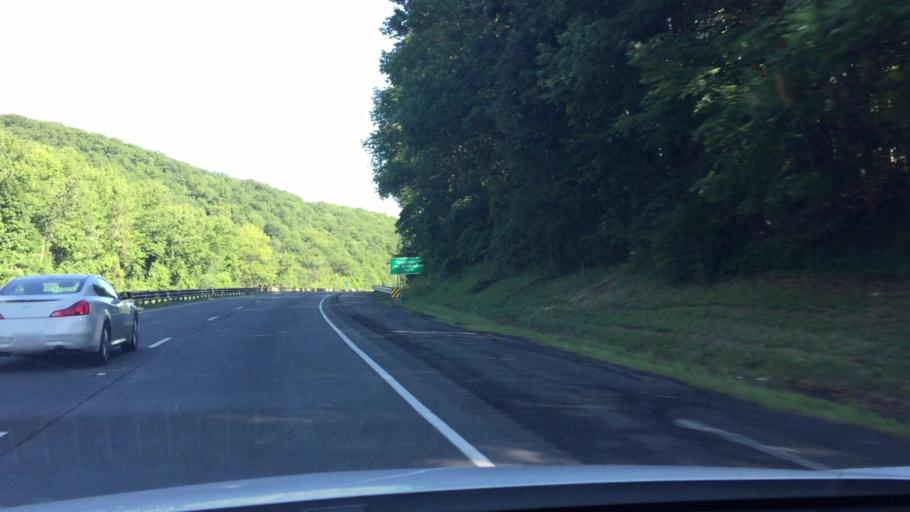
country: US
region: Massachusetts
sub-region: Berkshire County
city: West Stockbridge
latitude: 42.3106
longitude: -73.3564
